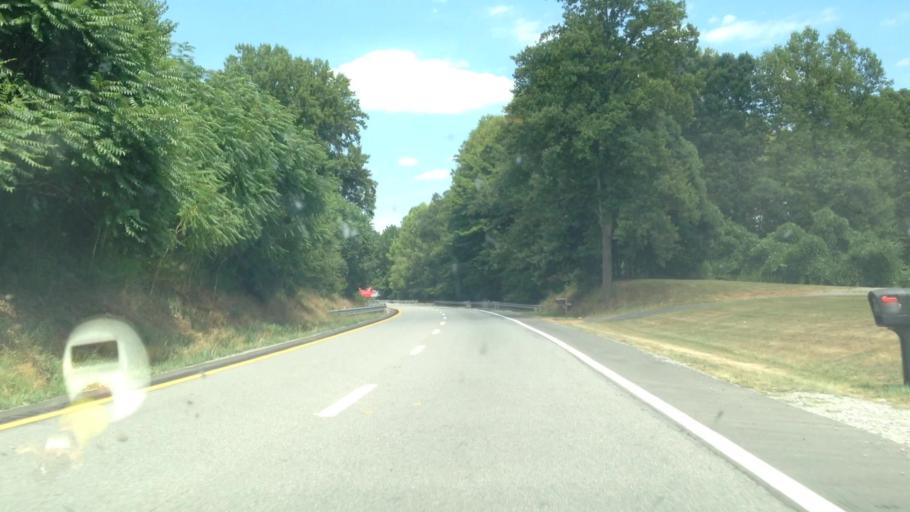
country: US
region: North Carolina
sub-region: Rockingham County
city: Stoneville
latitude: 36.5469
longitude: -79.9003
